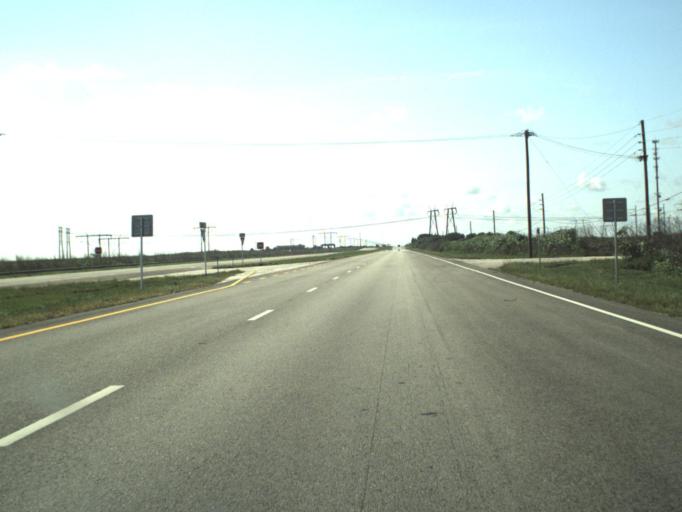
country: US
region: Florida
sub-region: Broward County
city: Weston
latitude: 26.3443
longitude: -80.5453
